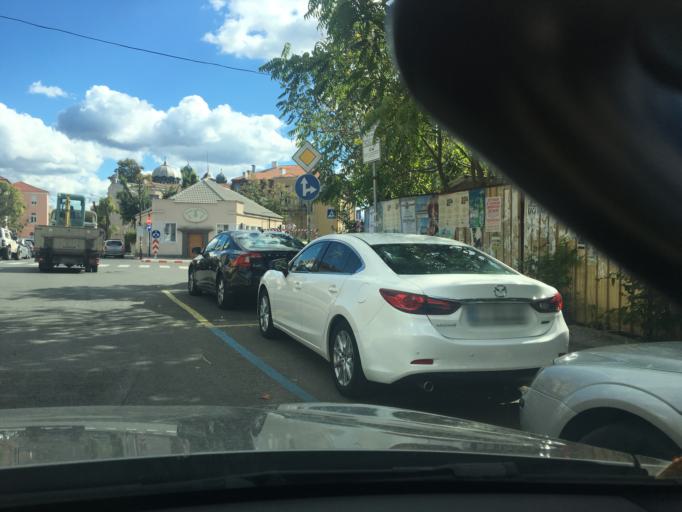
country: BG
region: Burgas
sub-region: Obshtina Burgas
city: Burgas
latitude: 42.4976
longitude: 27.4728
